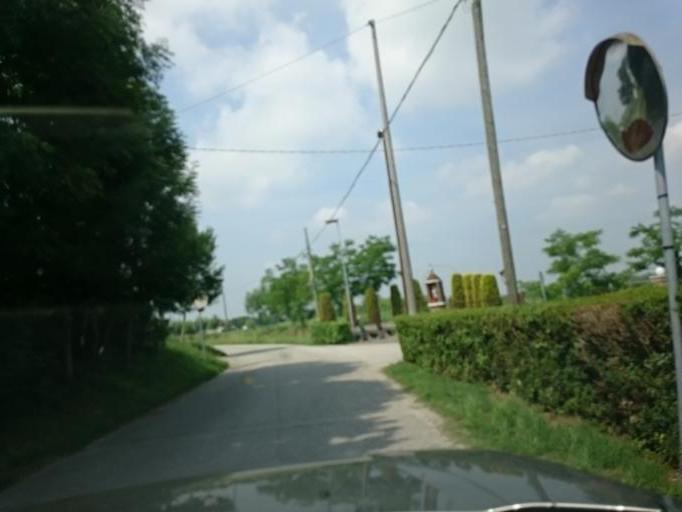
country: IT
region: Veneto
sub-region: Provincia di Padova
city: Codevigo
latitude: 45.2712
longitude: 12.1154
